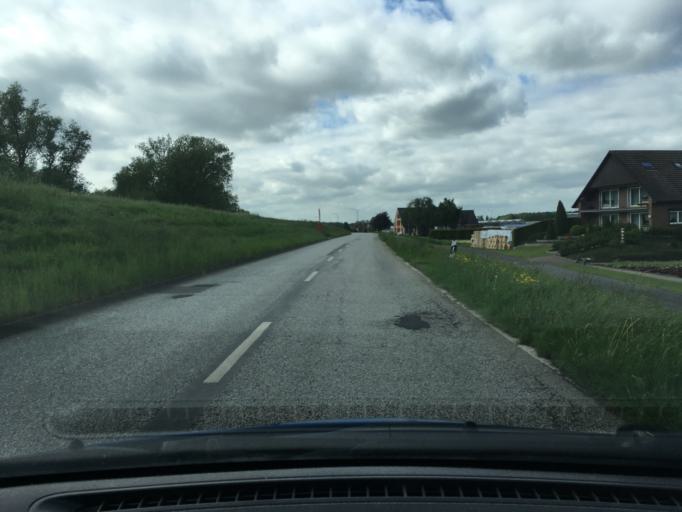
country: DE
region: Hamburg
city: Rothenburgsort
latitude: 53.4653
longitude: 10.0563
